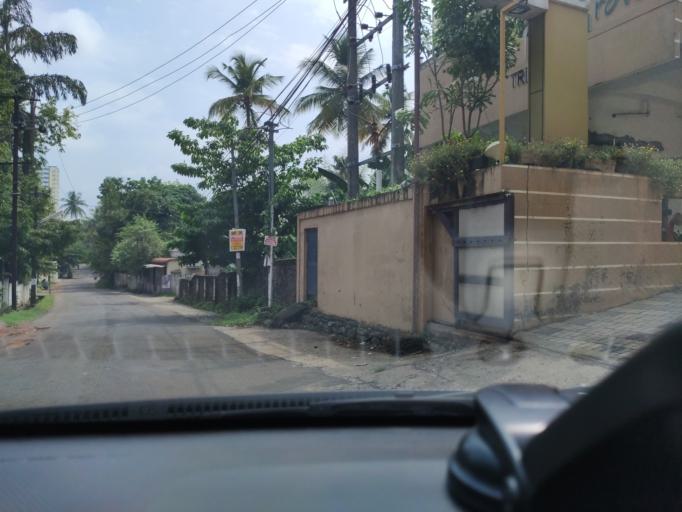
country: IN
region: Kerala
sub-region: Ernakulam
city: Elur
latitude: 10.0296
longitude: 76.3292
